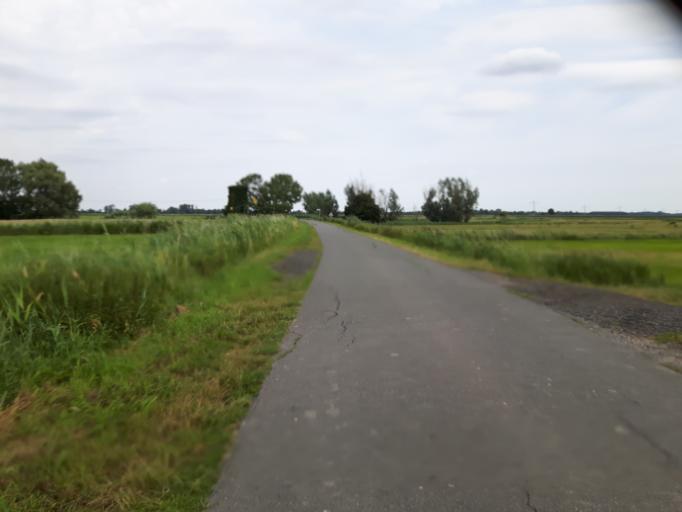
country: DE
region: Lower Saxony
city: Varel
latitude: 53.3715
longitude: 8.2098
